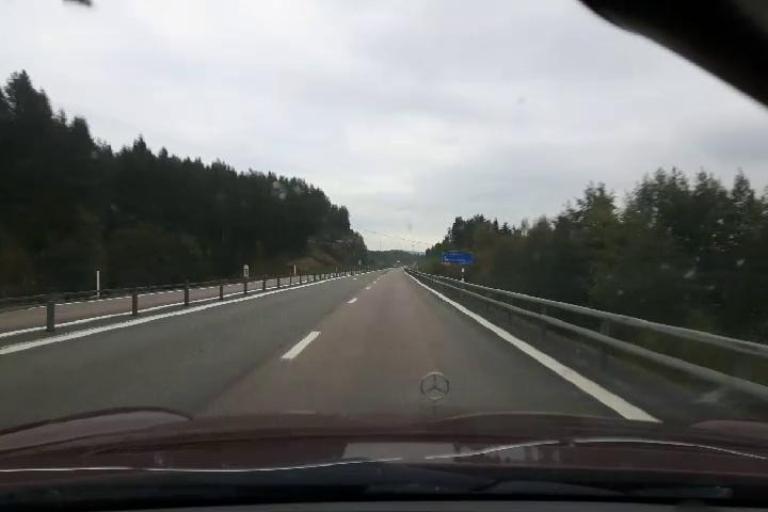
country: SE
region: Vaesternorrland
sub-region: Kramfors Kommun
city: Nordingra
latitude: 62.9260
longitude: 18.0984
